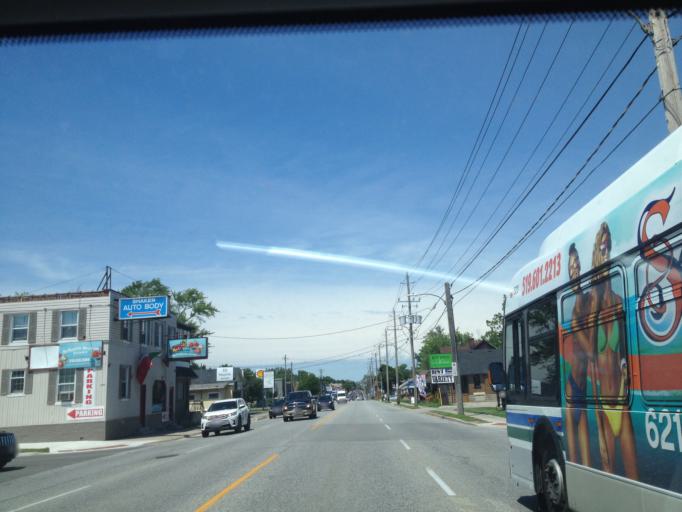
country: CA
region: Ontario
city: London
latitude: 42.9659
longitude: -81.2615
